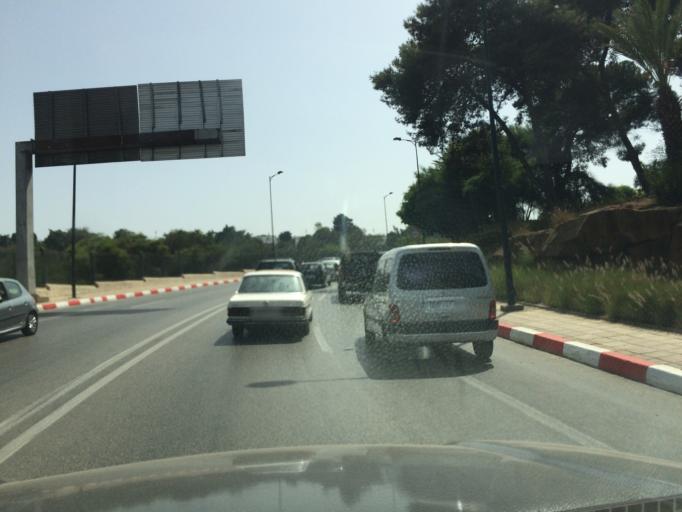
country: MA
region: Rabat-Sale-Zemmour-Zaer
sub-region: Rabat
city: Rabat
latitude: 34.0183
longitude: -6.8202
